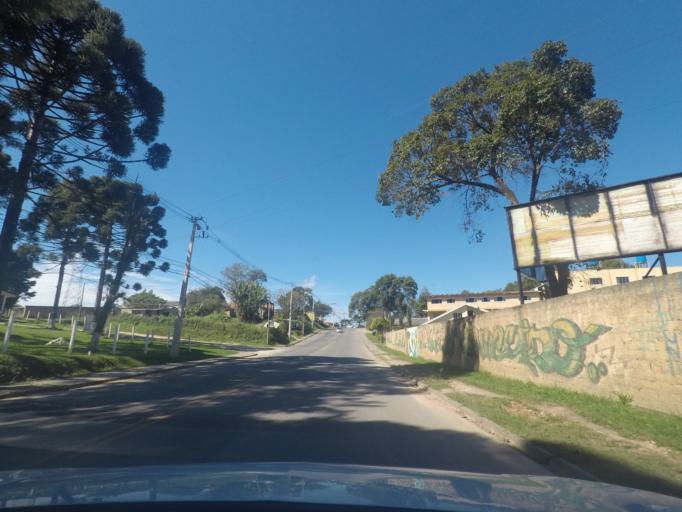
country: BR
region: Parana
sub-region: Almirante Tamandare
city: Almirante Tamandare
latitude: -25.3415
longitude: -49.3030
